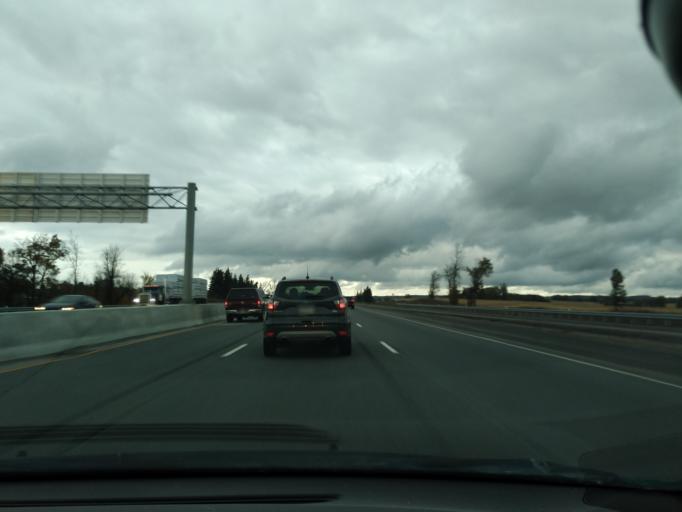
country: CA
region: Ontario
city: Bradford West Gwillimbury
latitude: 44.0802
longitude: -79.6257
